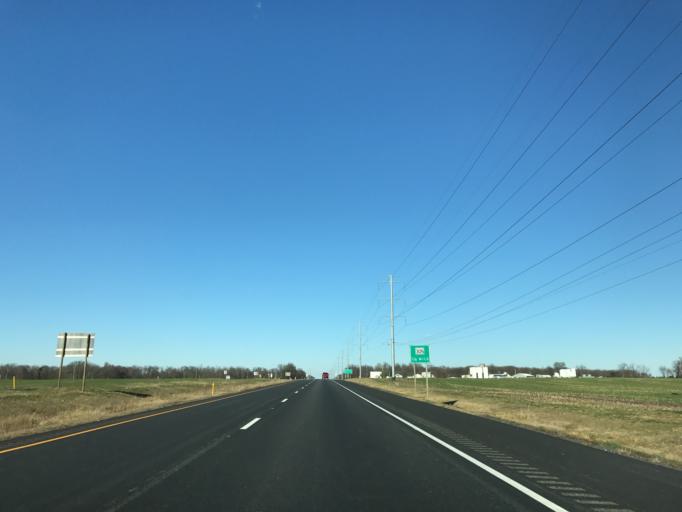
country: US
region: Maryland
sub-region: Queen Anne's County
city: Centreville
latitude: 39.0428
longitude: -76.0118
